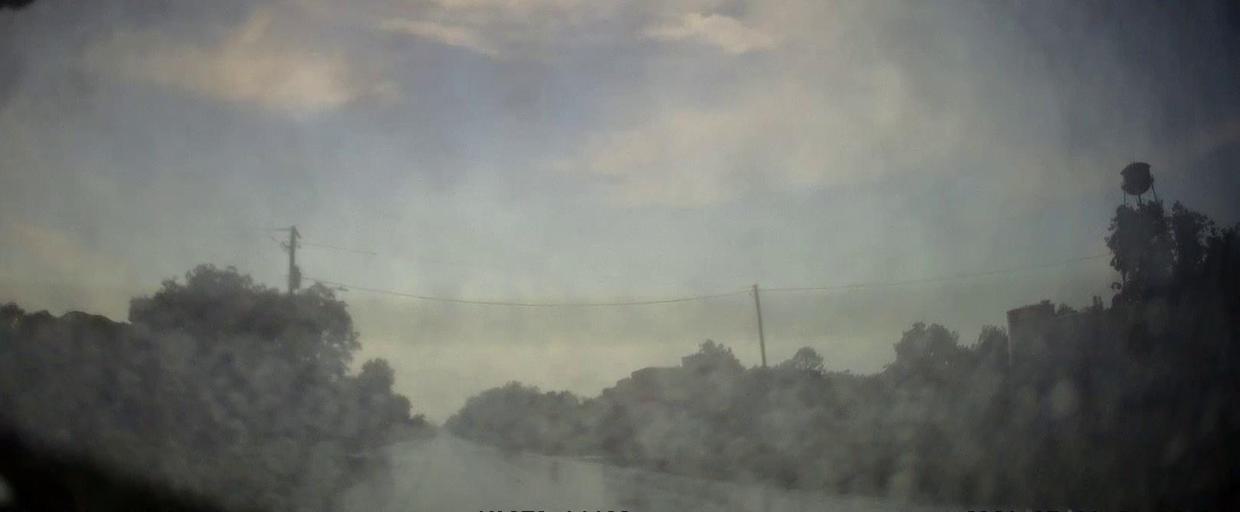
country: US
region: Georgia
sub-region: Dodge County
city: Chester
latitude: 32.5596
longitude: -83.1532
